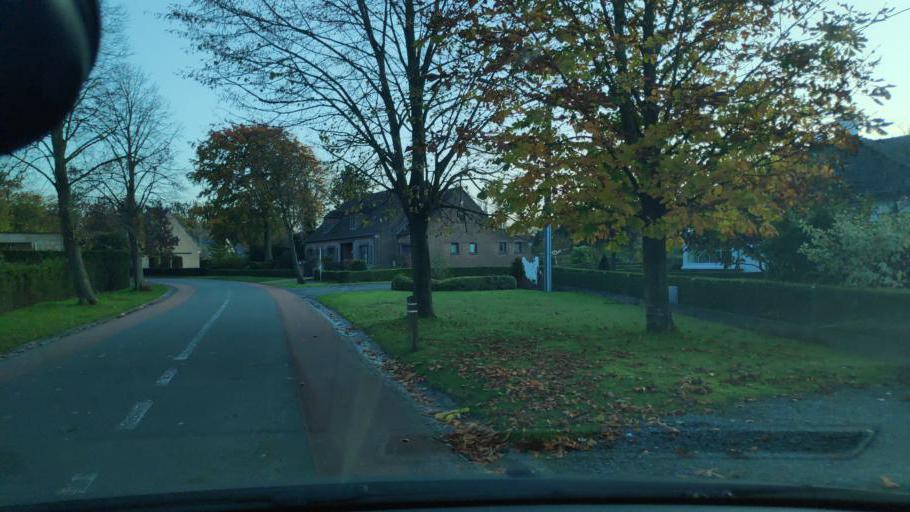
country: BE
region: Flanders
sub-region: Provincie Oost-Vlaanderen
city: Aalter
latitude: 51.0866
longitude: 3.4874
